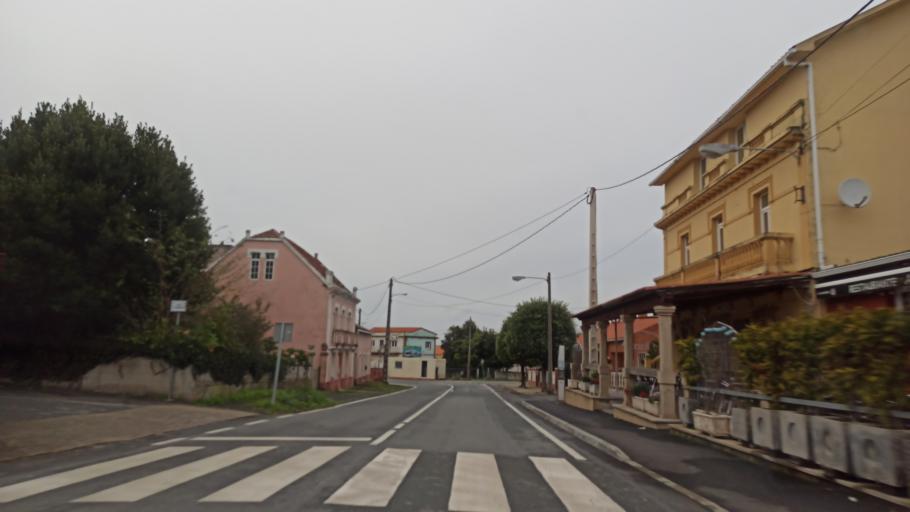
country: ES
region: Galicia
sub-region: Provincia da Coruna
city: Oleiros
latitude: 43.3905
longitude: -8.3091
